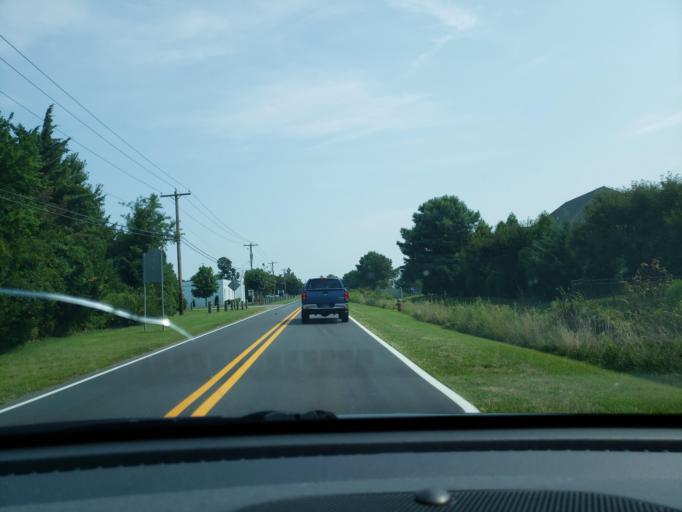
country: US
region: Delaware
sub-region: Sussex County
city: Lewes
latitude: 38.7755
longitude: -75.1570
